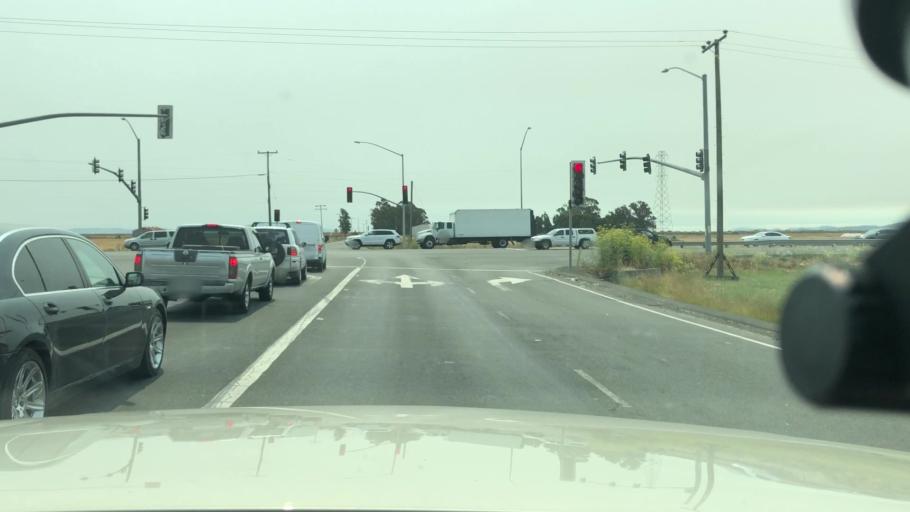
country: US
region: California
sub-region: Marin County
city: Black Point-Green Point
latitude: 38.1345
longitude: -122.4767
